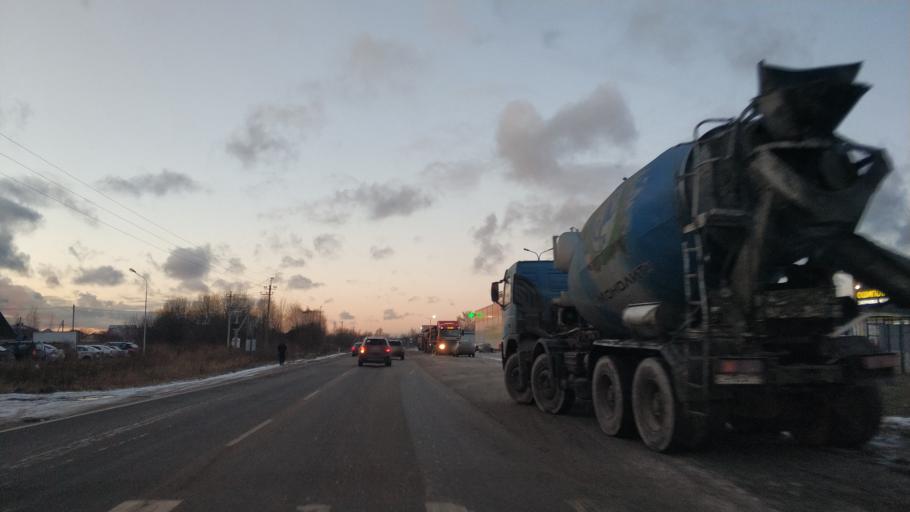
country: RU
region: St.-Petersburg
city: Pontonnyy
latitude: 59.8015
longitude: 30.6337
